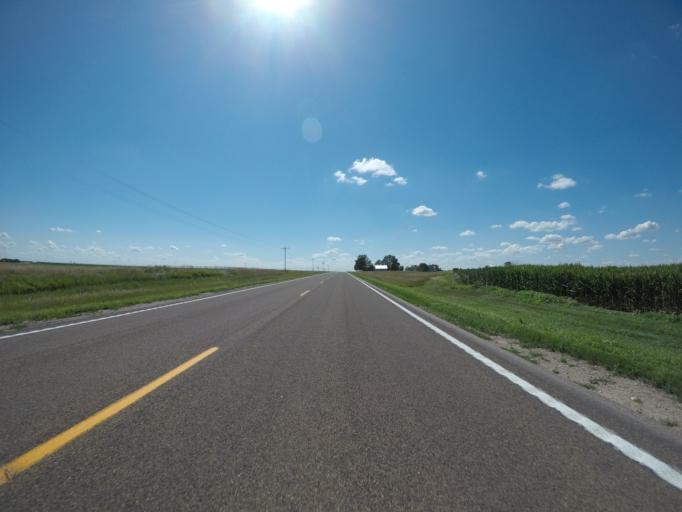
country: US
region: Nebraska
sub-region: Chase County
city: Imperial
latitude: 40.5376
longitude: -101.8517
